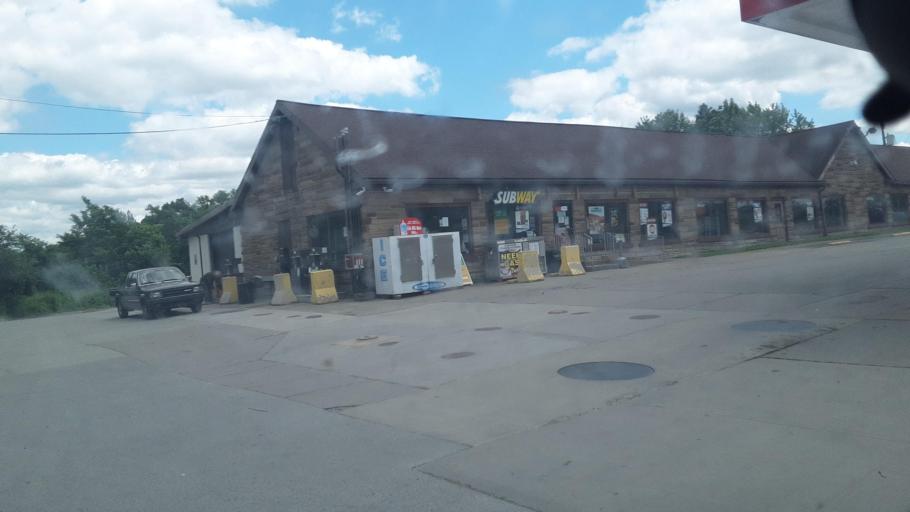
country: US
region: Pennsylvania
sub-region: Butler County
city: Prospect
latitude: 40.9507
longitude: -80.1540
